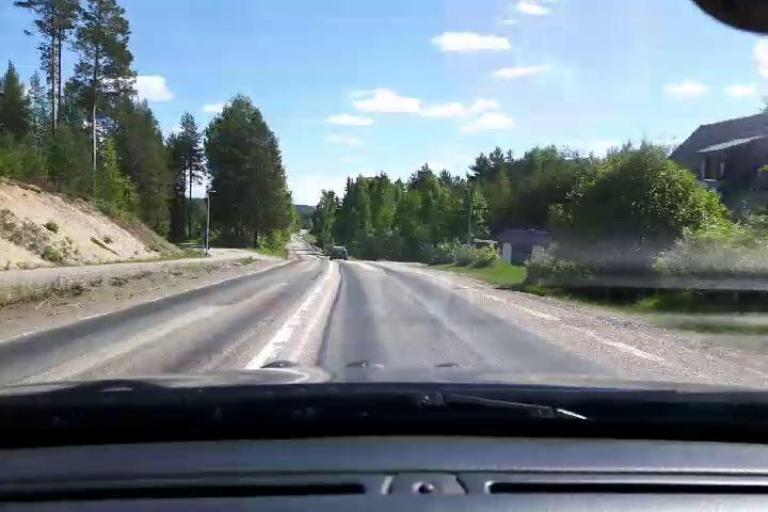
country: SE
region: Gaevleborg
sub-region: Ljusdals Kommun
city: Farila
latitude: 61.9812
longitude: 15.3172
